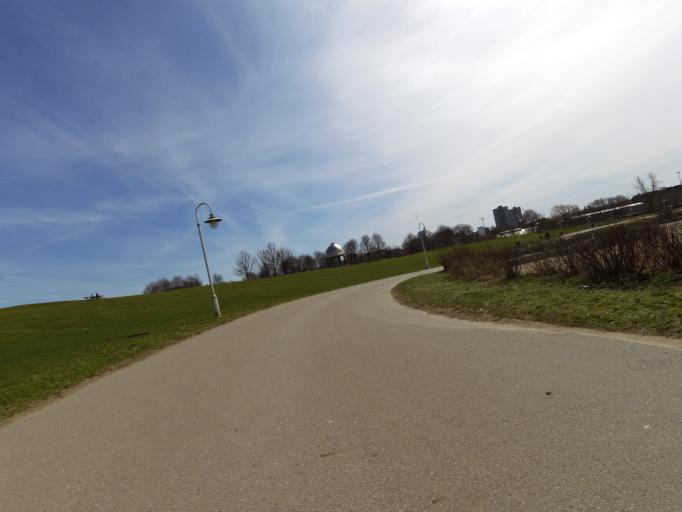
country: CA
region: Ontario
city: Hamilton
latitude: 43.2722
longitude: -79.8739
